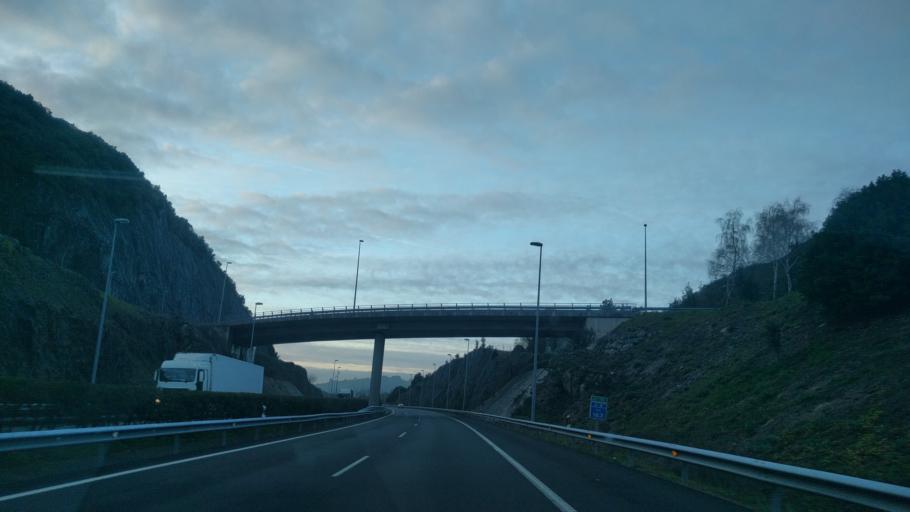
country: ES
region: Cantabria
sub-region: Provincia de Cantabria
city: Liendo
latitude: 43.3898
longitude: -3.3498
